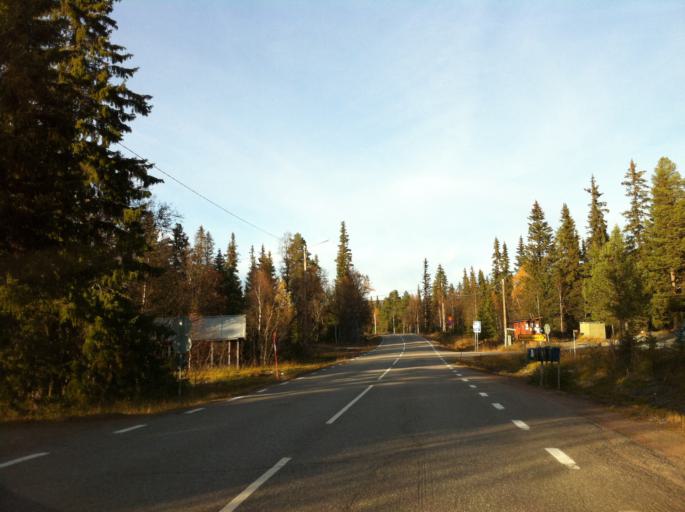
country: NO
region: Hedmark
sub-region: Engerdal
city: Engerdal
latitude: 62.0703
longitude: 12.3116
